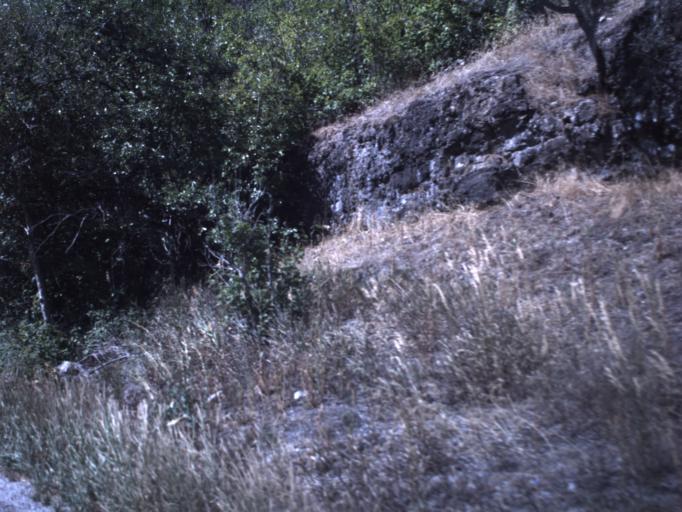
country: US
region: Utah
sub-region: Cache County
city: North Logan
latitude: 41.7871
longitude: -111.6429
